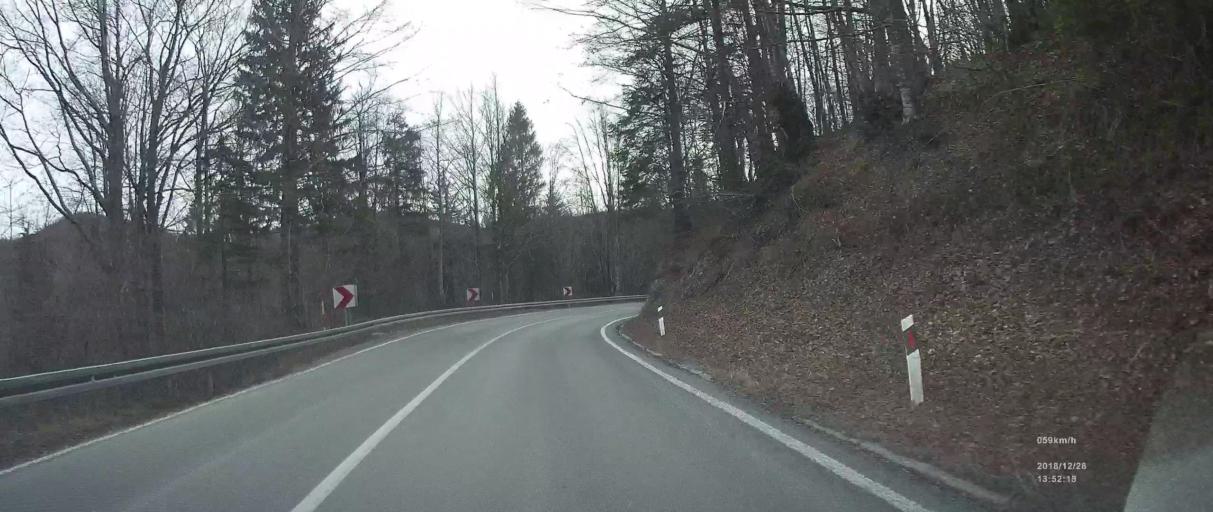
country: HR
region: Primorsko-Goranska
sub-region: Grad Delnice
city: Delnice
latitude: 45.3916
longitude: 14.8468
